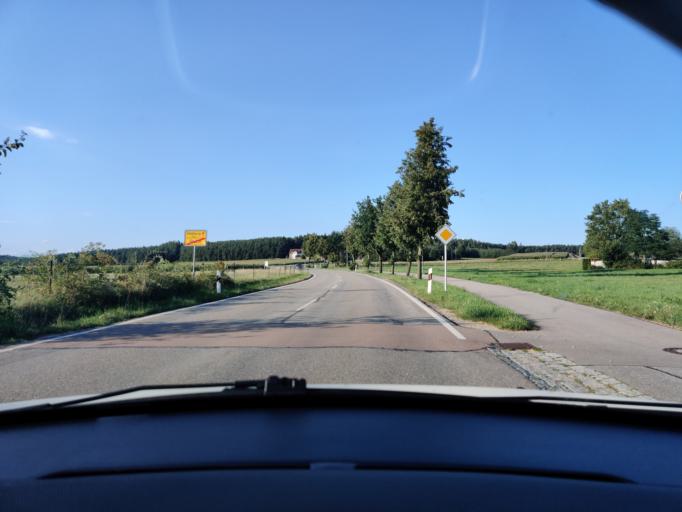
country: DE
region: Bavaria
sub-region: Upper Palatinate
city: Stulln
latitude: 49.4229
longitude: 12.1382
